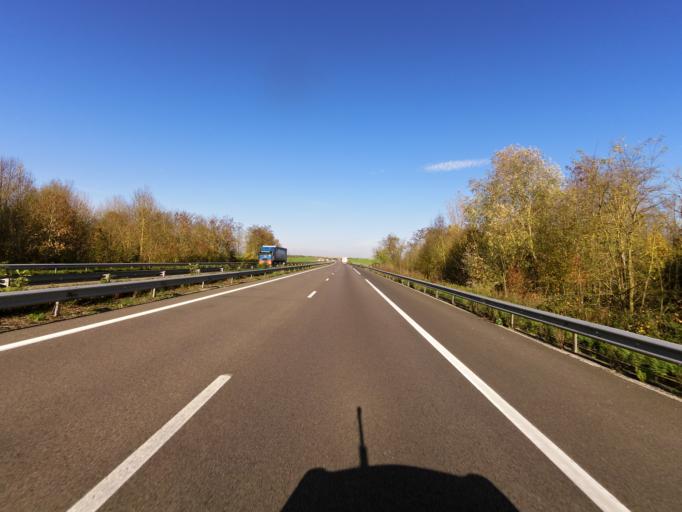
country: FR
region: Champagne-Ardenne
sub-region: Departement de la Marne
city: Fagnieres
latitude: 49.0219
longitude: 4.2901
